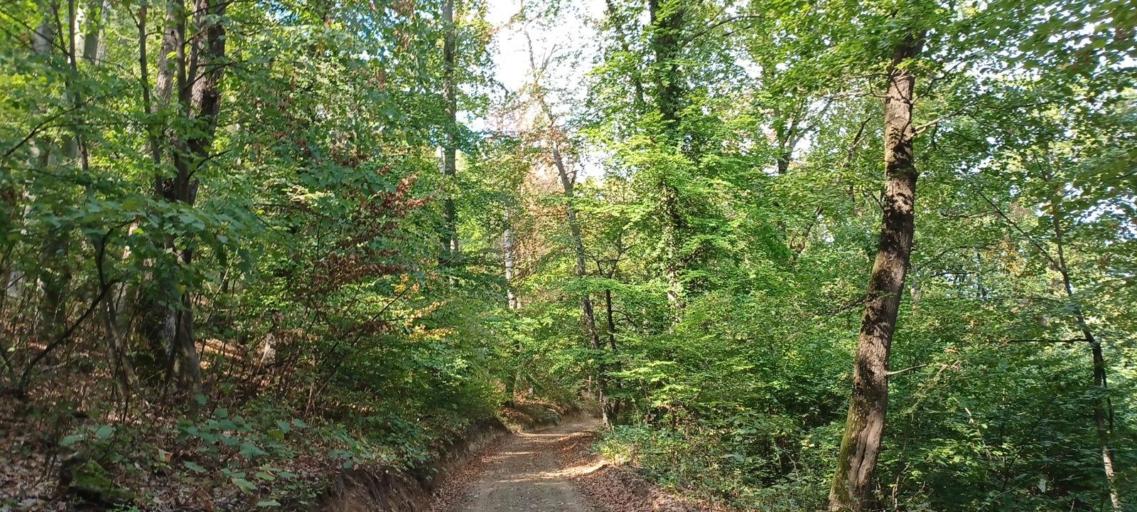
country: HU
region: Tolna
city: Szentgalpuszta
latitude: 46.3229
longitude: 18.6255
